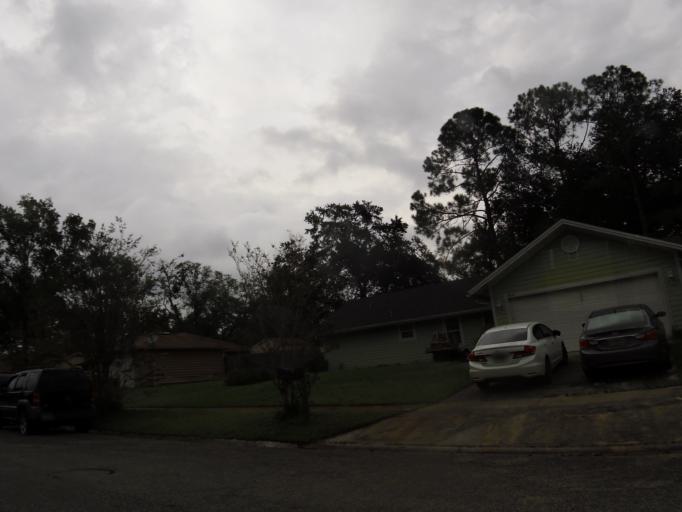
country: US
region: Florida
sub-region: Clay County
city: Bellair-Meadowbrook Terrace
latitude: 30.1939
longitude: -81.7654
